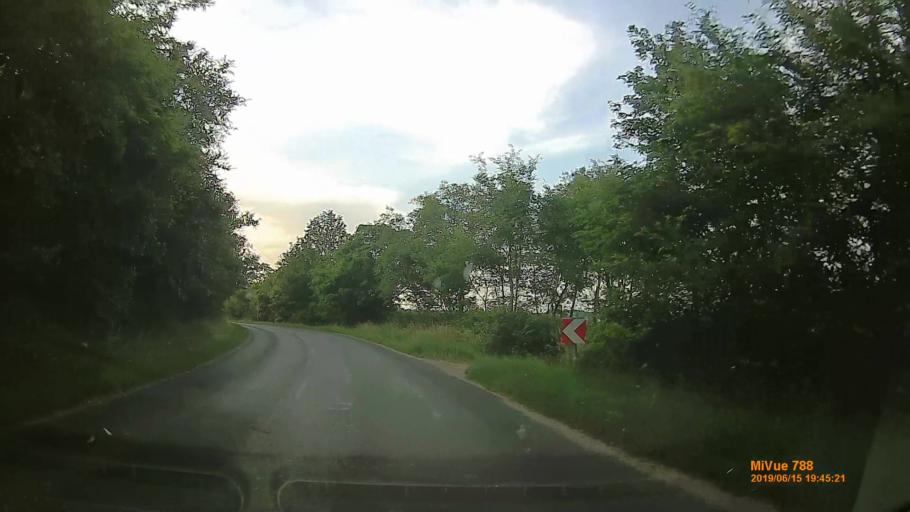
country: HU
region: Veszprem
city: Szentkiralyszabadja
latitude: 47.0087
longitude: 17.9654
